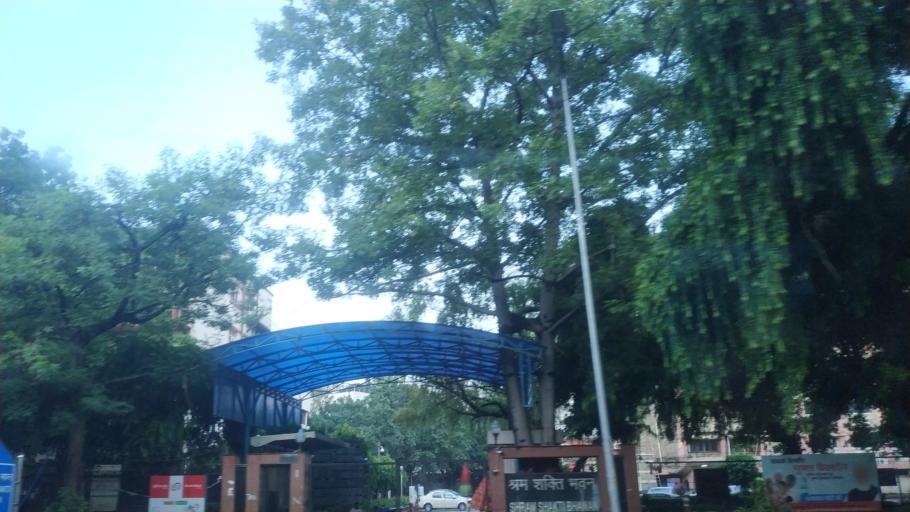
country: IN
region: NCT
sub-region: New Delhi
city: New Delhi
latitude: 28.6189
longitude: 77.2125
